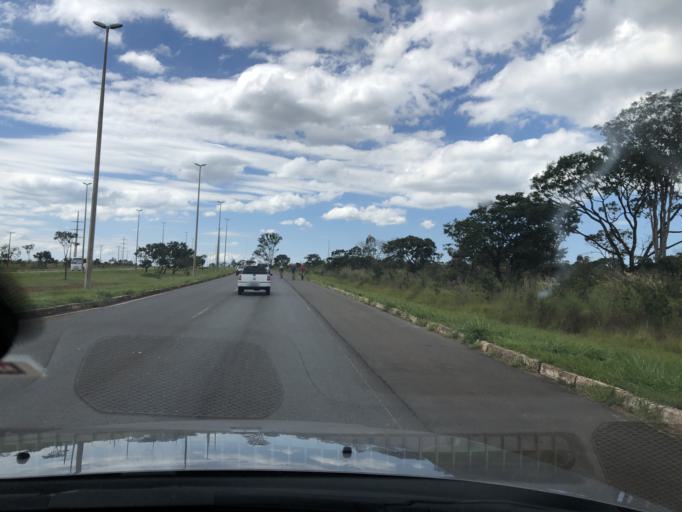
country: BR
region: Federal District
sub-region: Brasilia
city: Brasilia
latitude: -15.9784
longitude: -48.0001
